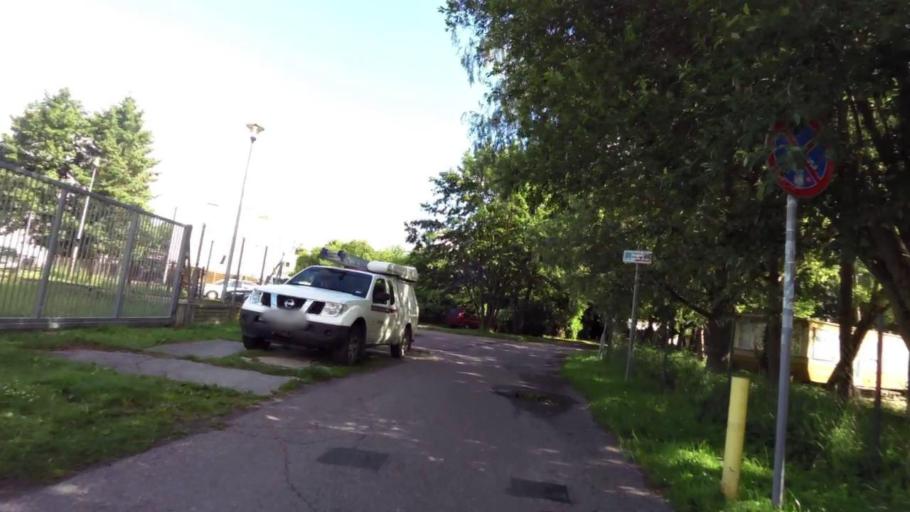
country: PL
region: West Pomeranian Voivodeship
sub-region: Powiat koszalinski
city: Mielno
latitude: 54.2582
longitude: 16.0575
